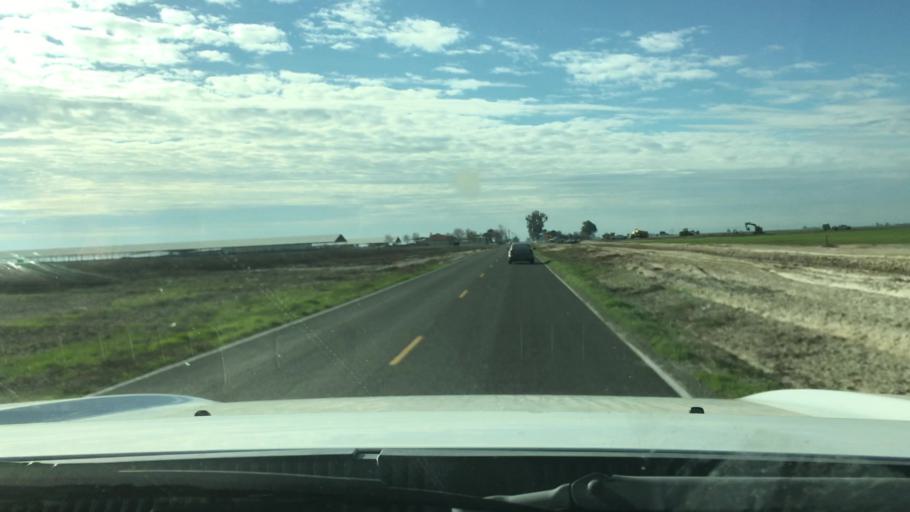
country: US
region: California
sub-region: Kings County
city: Stratford
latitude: 36.2144
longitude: -119.7624
